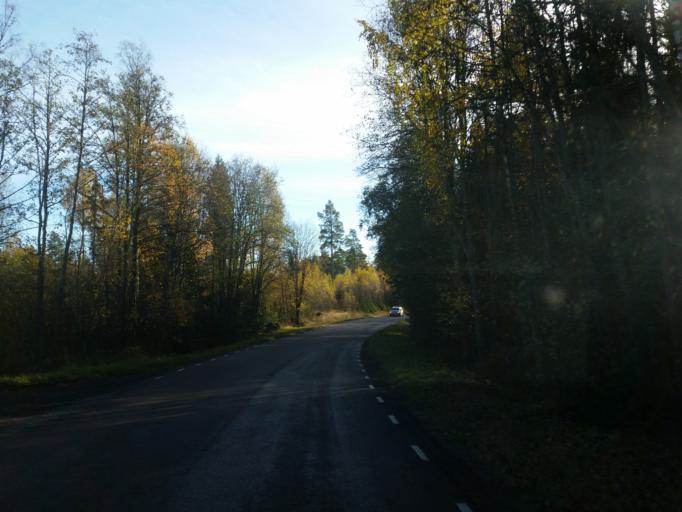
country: SE
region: Dalarna
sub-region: Borlange Kommun
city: Ornas
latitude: 60.5156
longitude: 15.5221
